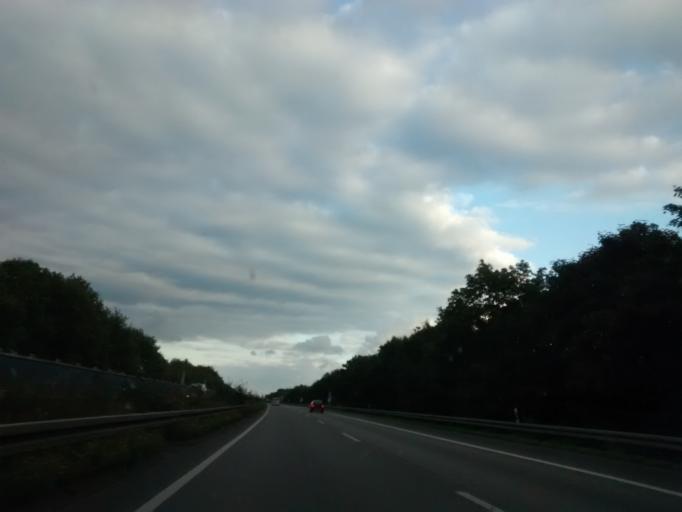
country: DE
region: North Rhine-Westphalia
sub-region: Regierungsbezirk Munster
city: Horstel
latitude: 52.2874
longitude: 7.5865
